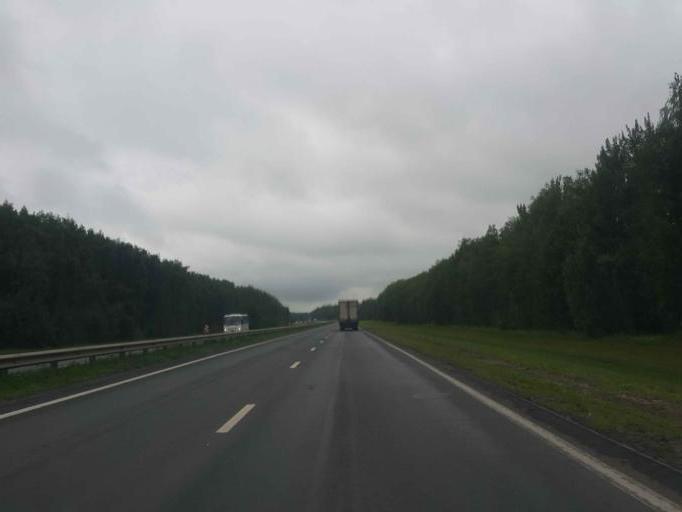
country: RU
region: Tambov
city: Selezni
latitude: 52.7646
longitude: 41.1110
